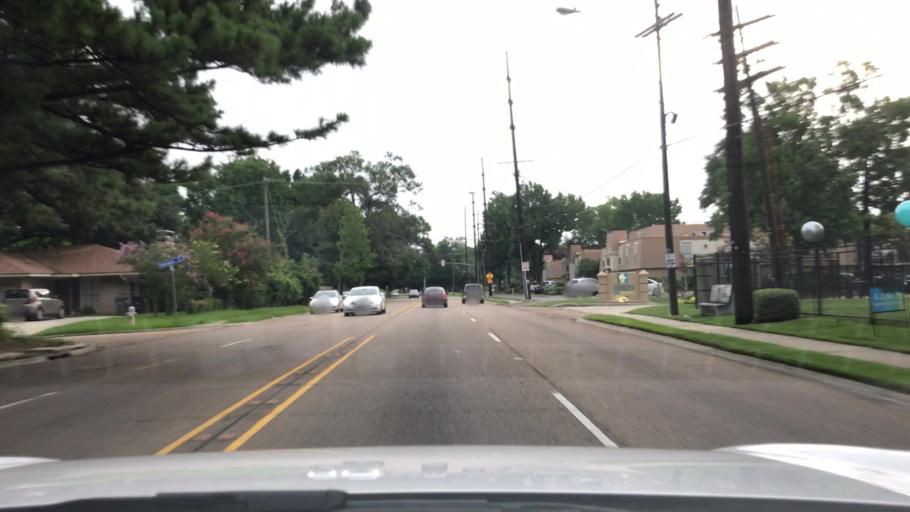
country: US
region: Louisiana
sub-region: East Baton Rouge Parish
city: Baton Rouge
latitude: 30.4280
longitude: -91.1365
